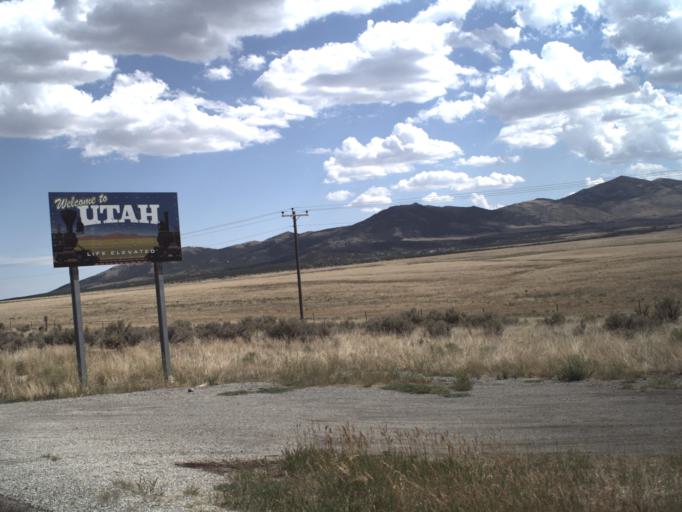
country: US
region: Idaho
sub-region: Minidoka County
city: Rupert
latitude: 41.9976
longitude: -113.1932
